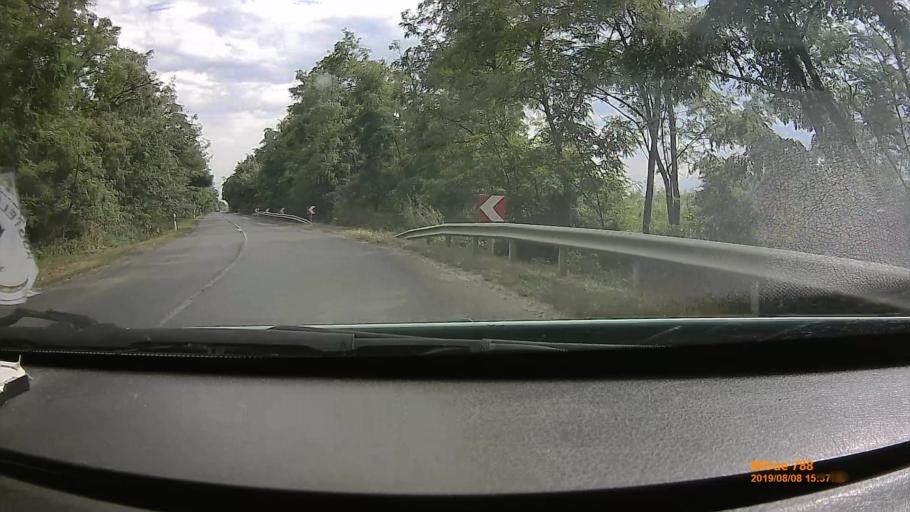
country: HU
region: Szabolcs-Szatmar-Bereg
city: Kocsord
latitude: 47.9467
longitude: 22.4270
